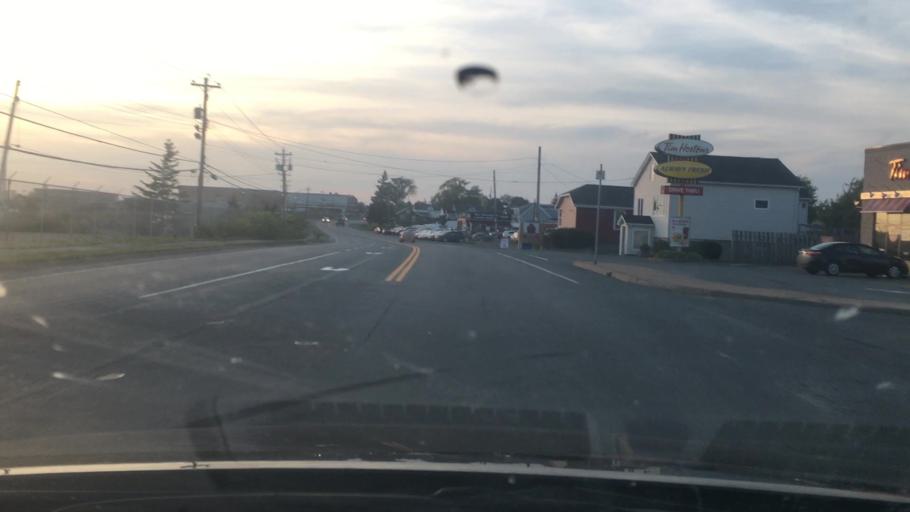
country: CA
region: Nova Scotia
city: Cole Harbour
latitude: 44.6234
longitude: -63.5101
